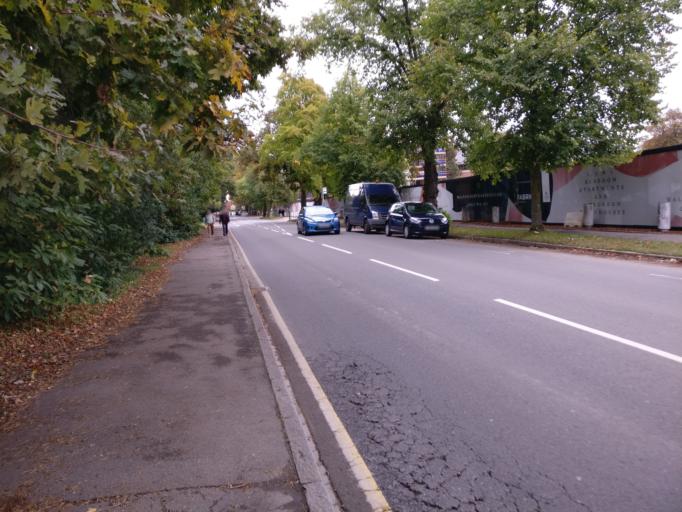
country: GB
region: England
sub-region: Surrey
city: Walton-on-Thames
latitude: 51.3747
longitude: -0.4122
